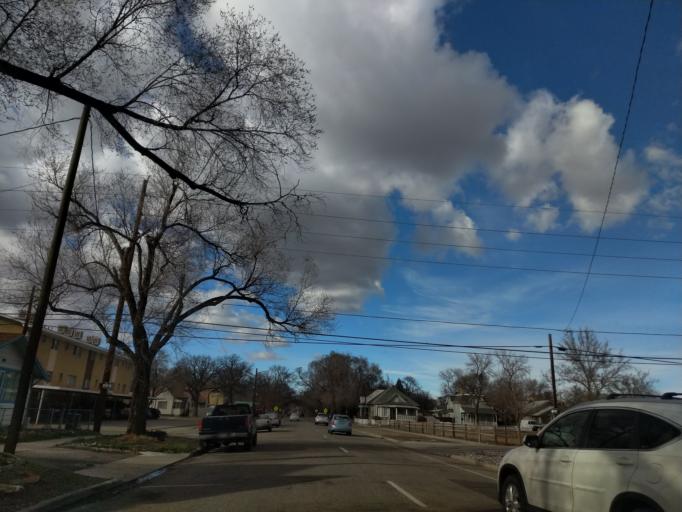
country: US
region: Colorado
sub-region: Mesa County
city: Grand Junction
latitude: 39.0716
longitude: -108.5645
